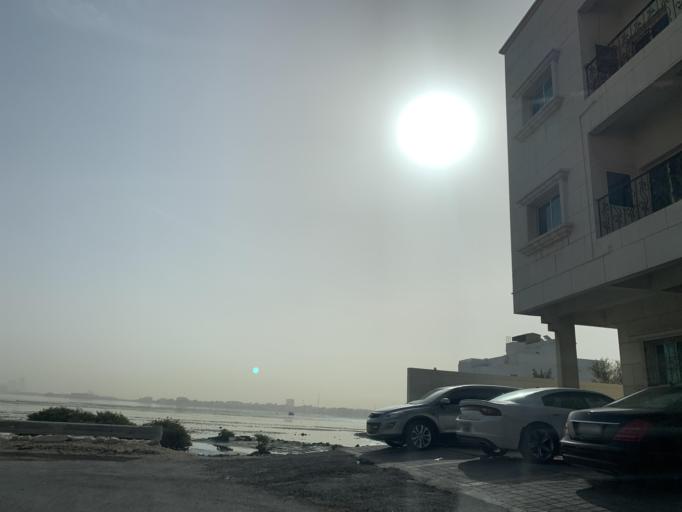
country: BH
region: Northern
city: Madinat `Isa
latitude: 26.1810
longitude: 50.5659
